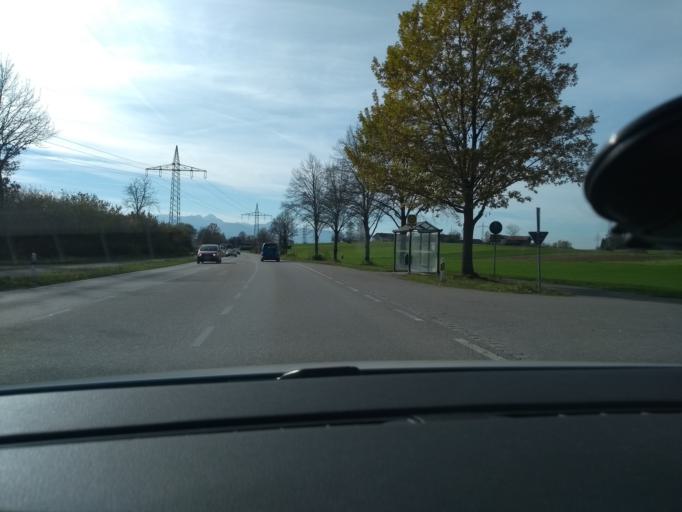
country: DE
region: Bavaria
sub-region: Upper Bavaria
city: Stephanskirchen
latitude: 47.8779
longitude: 12.1782
